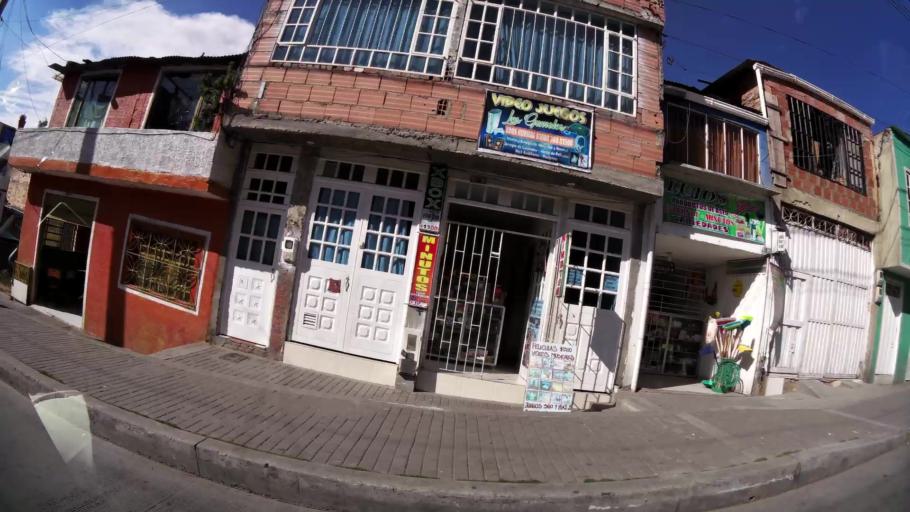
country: CO
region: Cundinamarca
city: Soacha
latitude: 4.5563
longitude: -74.1457
